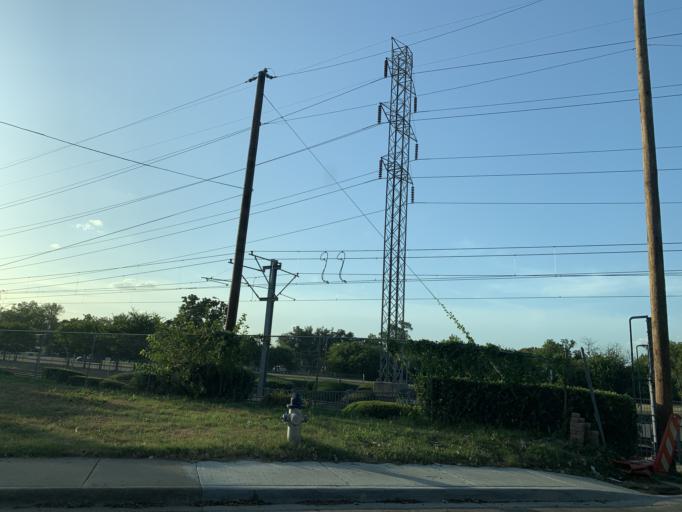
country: US
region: Texas
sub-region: Dallas County
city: Dallas
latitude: 32.7662
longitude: -96.7432
